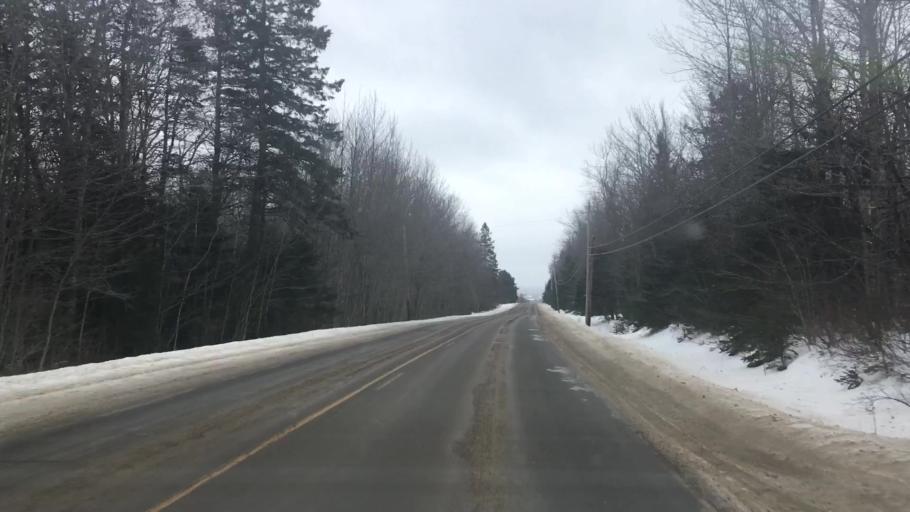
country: US
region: Maine
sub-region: Washington County
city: East Machias
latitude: 44.9843
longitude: -67.4563
